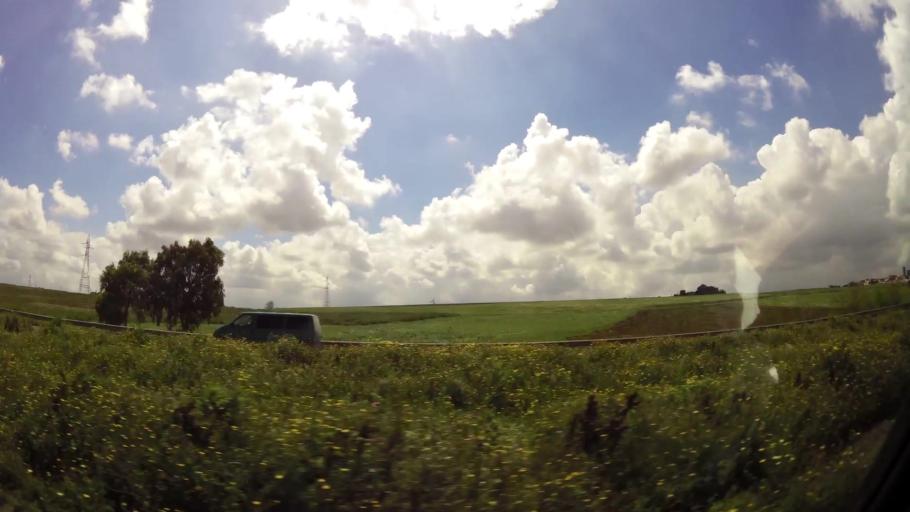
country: MA
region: Grand Casablanca
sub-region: Mediouna
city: Tit Mellil
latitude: 33.5477
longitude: -7.5234
